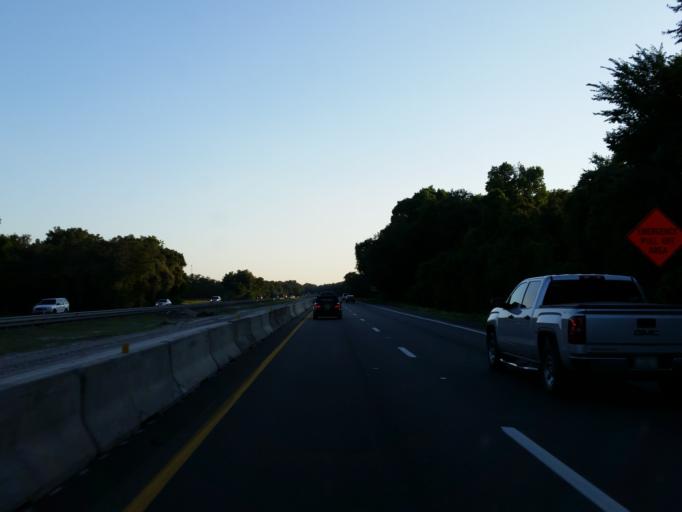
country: US
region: Florida
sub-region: Sumter County
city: Bushnell
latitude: 28.6164
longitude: -82.1885
